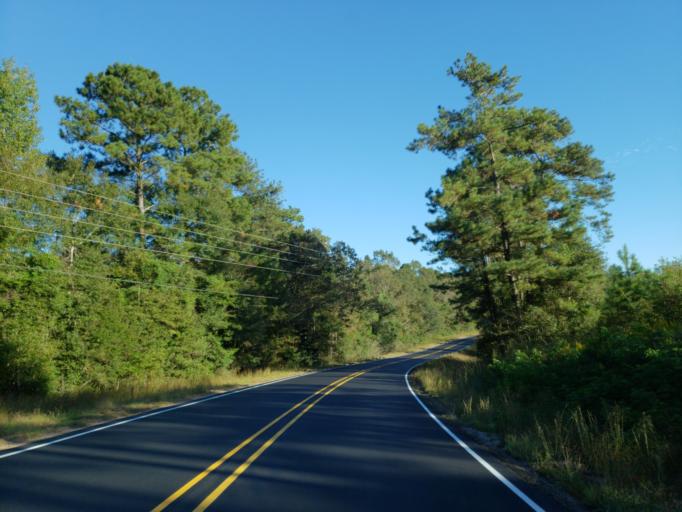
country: US
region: Mississippi
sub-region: Perry County
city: Richton
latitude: 31.3559
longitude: -88.7883
